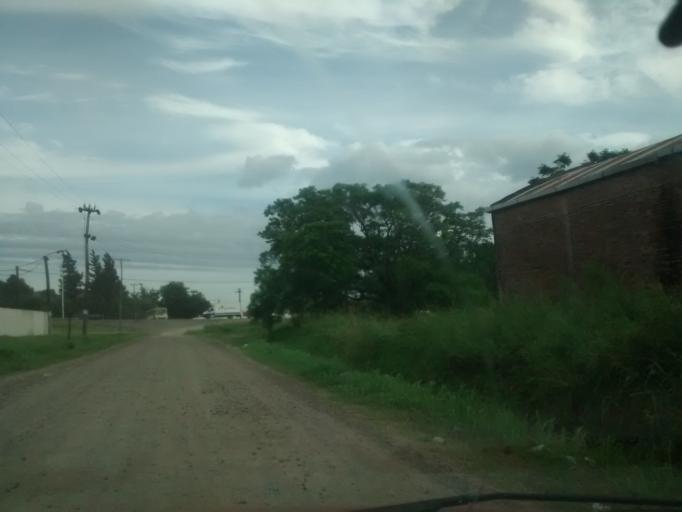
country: AR
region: Chaco
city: Fontana
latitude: -27.4585
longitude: -59.0356
